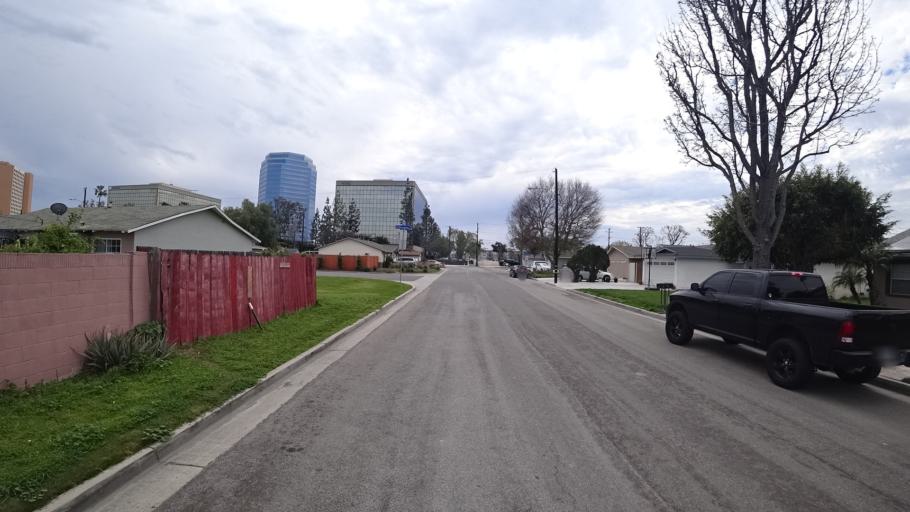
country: US
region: California
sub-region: Orange County
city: Orange
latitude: 33.7900
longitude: -117.8955
